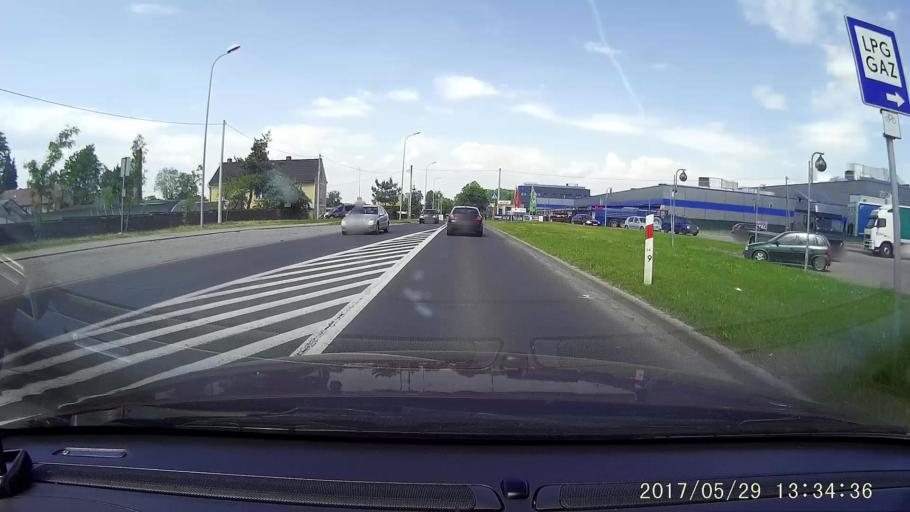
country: PL
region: Lower Silesian Voivodeship
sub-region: Powiat lubanski
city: Luban
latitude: 51.1049
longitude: 15.3046
